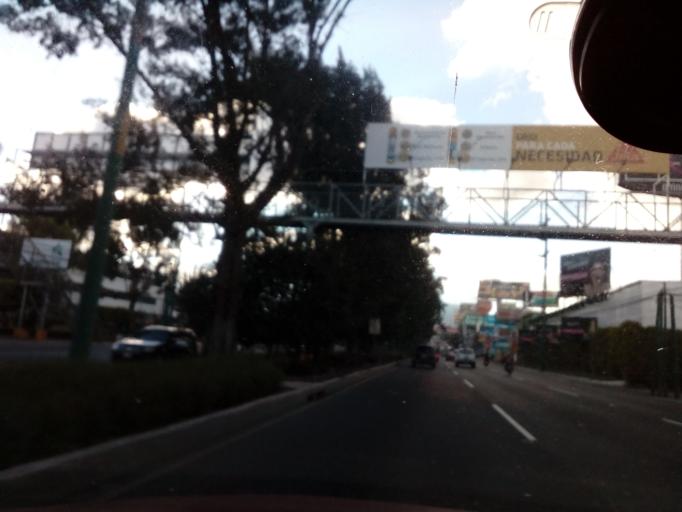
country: GT
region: Guatemala
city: Mixco
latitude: 14.6340
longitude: -90.5764
